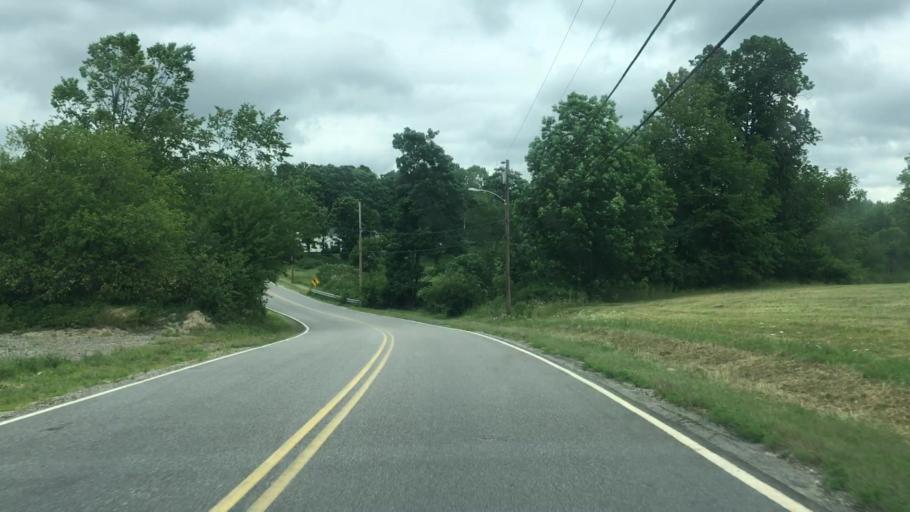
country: US
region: Maine
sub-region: York County
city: Biddeford
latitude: 43.5181
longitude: -70.5130
